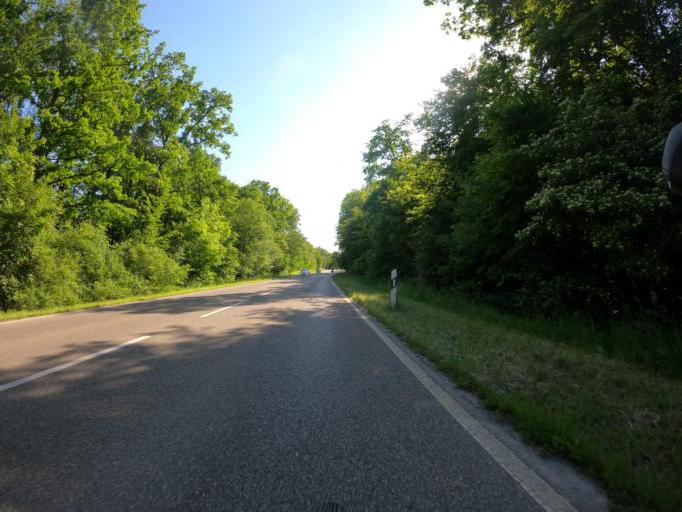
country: DE
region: Baden-Wuerttemberg
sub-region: Regierungsbezirk Stuttgart
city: Magstadt
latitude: 48.7328
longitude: 8.9926
